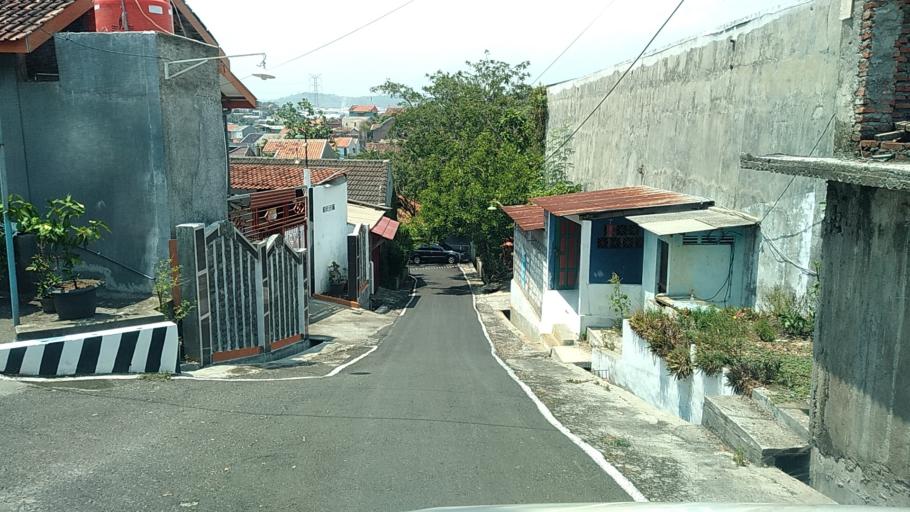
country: ID
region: Central Java
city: Semarang
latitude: -6.9956
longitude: 110.3625
